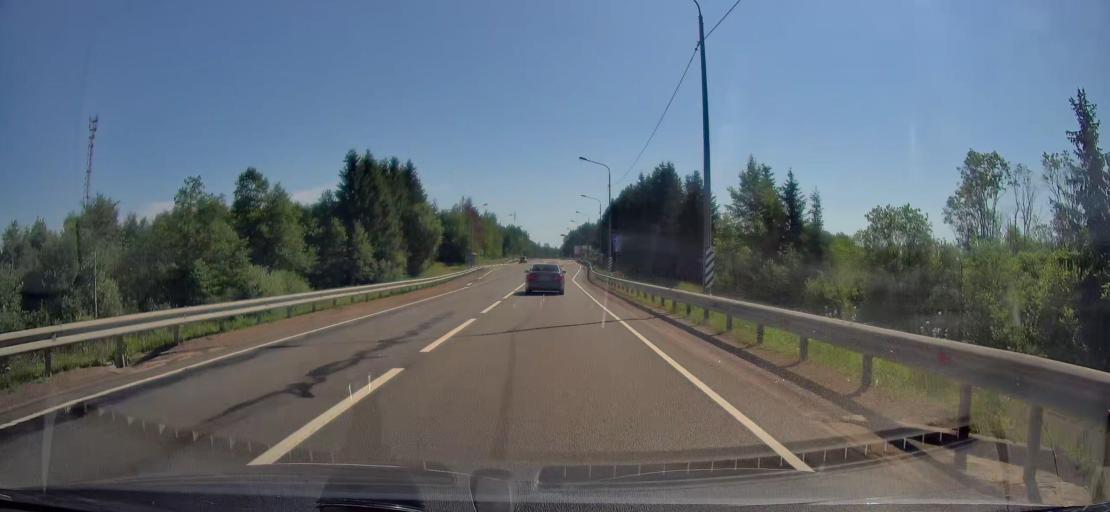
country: RU
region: Leningrad
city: Yefimovskiy
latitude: 59.3468
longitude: 34.8537
